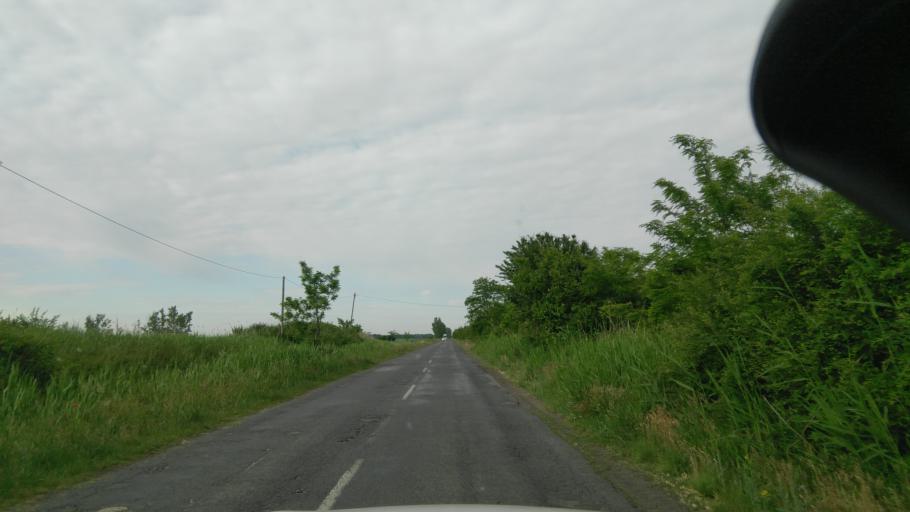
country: HU
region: Bekes
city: Elek
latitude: 46.5789
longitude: 21.2190
